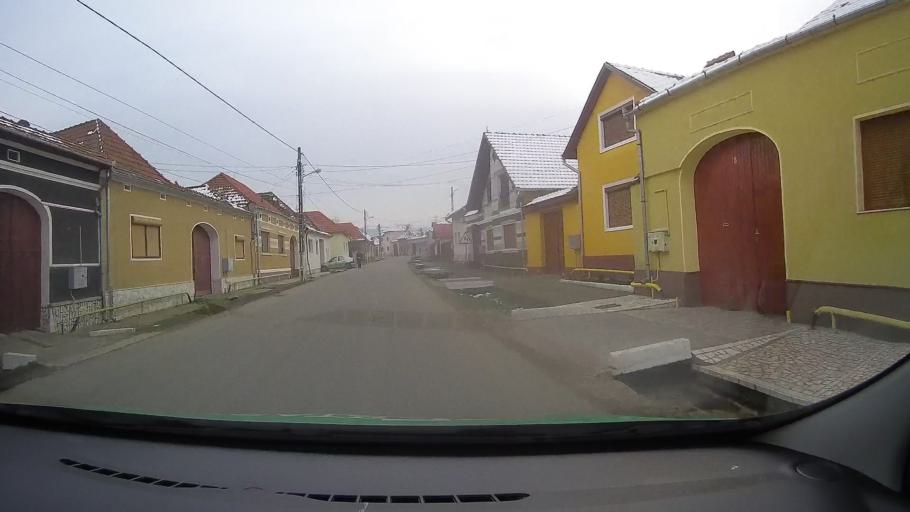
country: RO
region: Hunedoara
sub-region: Comuna Romos
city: Romos
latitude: 45.8443
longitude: 23.2737
